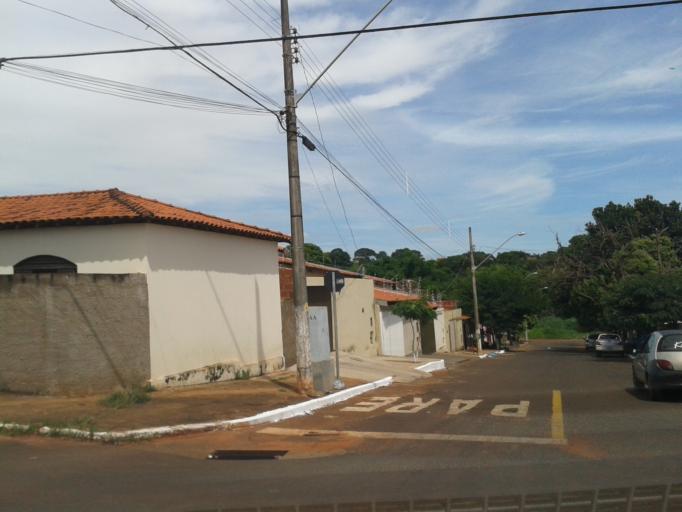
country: BR
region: Minas Gerais
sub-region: Santa Vitoria
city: Santa Vitoria
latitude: -18.8418
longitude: -50.1290
